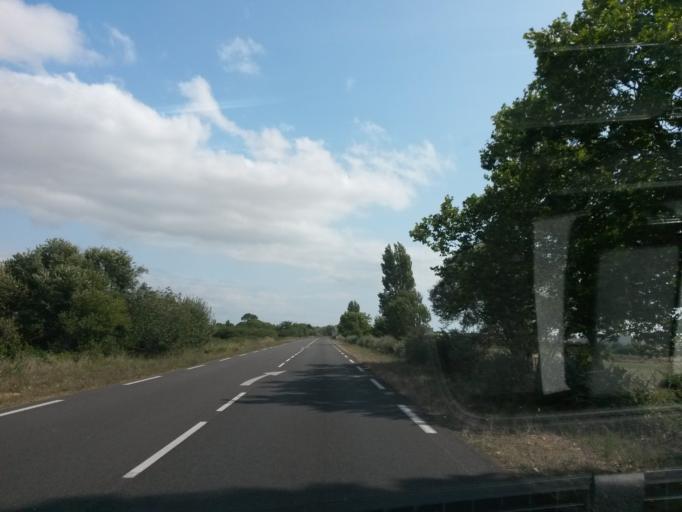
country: FR
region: Pays de la Loire
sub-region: Departement de la Vendee
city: La Tranche-sur-Mer
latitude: 46.3553
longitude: -1.4381
